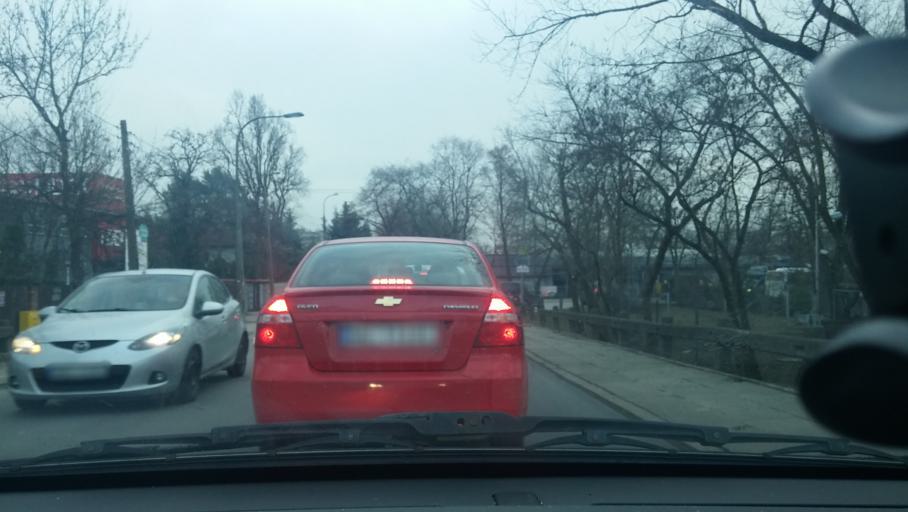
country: PL
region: Masovian Voivodeship
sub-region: Warszawa
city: Rembertow
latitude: 52.2259
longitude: 21.1494
